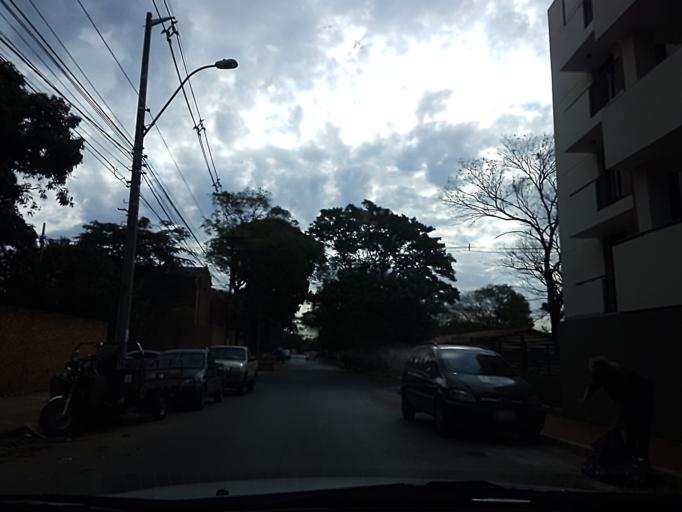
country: PY
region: Central
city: Lambare
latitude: -25.3007
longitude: -57.5835
